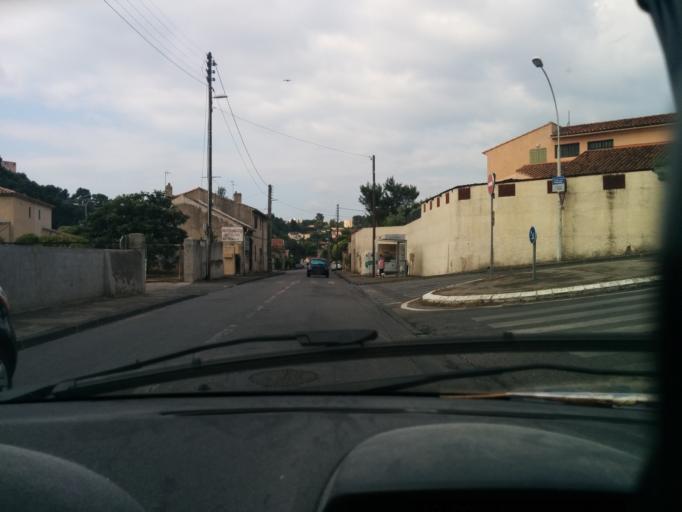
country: FR
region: Provence-Alpes-Cote d'Azur
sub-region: Departement des Bouches-du-Rhone
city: Plan-de-Cuques
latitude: 43.3254
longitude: 5.4508
